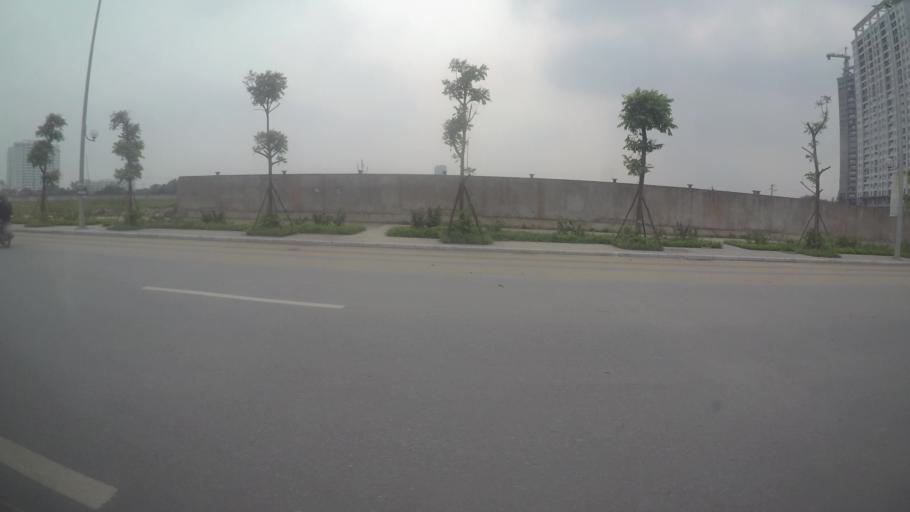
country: VN
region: Ha Noi
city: Cau Dien
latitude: 21.0465
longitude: 105.7362
